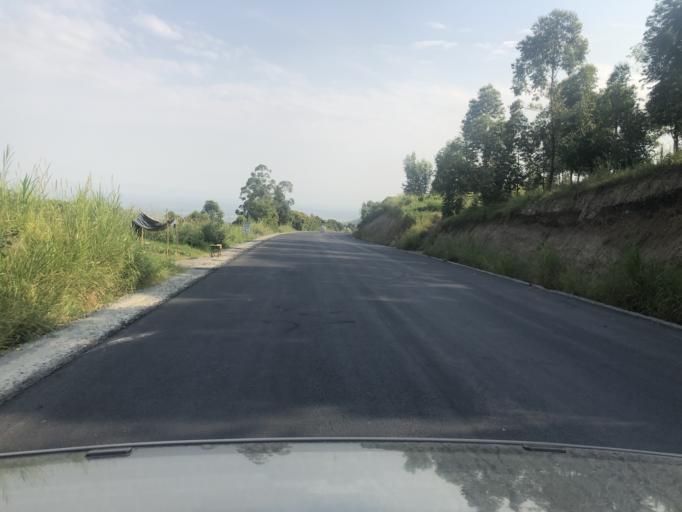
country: UG
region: Western Region
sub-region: Rubirizi District
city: Rubirizi
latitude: -0.2544
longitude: 30.0909
